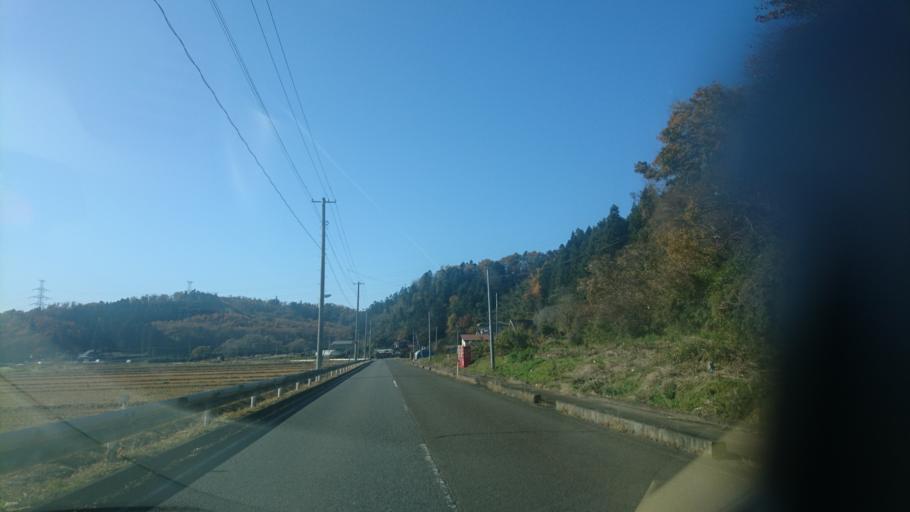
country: JP
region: Miyagi
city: Tomiya
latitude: 38.4063
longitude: 140.8693
